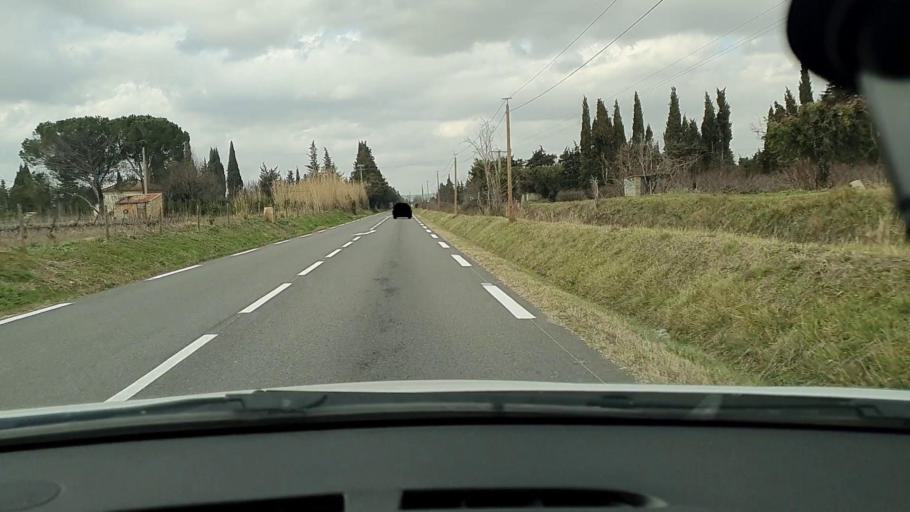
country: FR
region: Languedoc-Roussillon
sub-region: Departement du Gard
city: Montfrin
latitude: 43.8718
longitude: 4.5831
